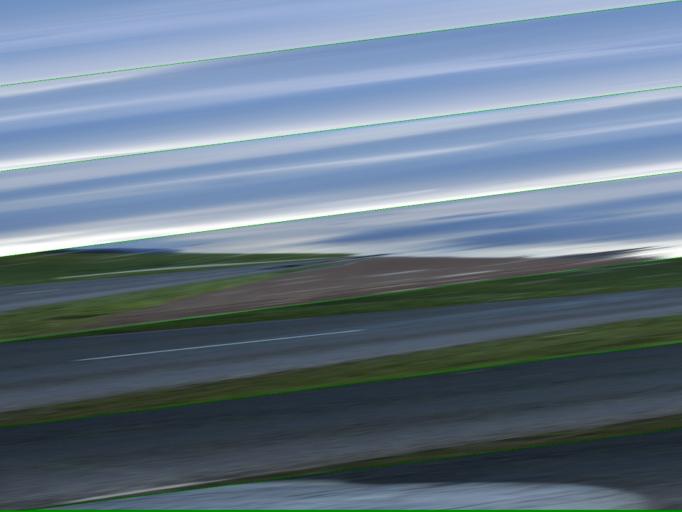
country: FR
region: Picardie
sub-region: Departement de l'Oise
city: Chaumont-en-Vexin
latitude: 49.3327
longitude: 1.9091
